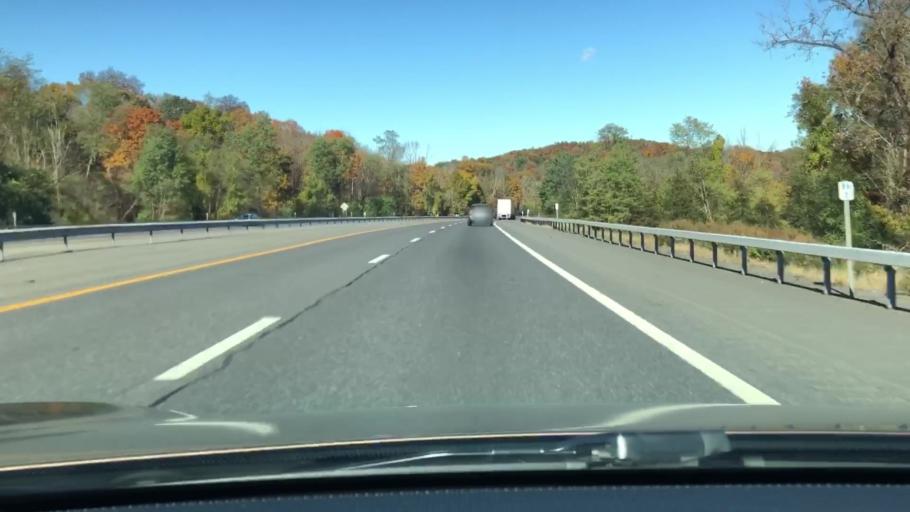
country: US
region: New York
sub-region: Ulster County
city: Rosendale Village
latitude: 41.8814
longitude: -74.0581
